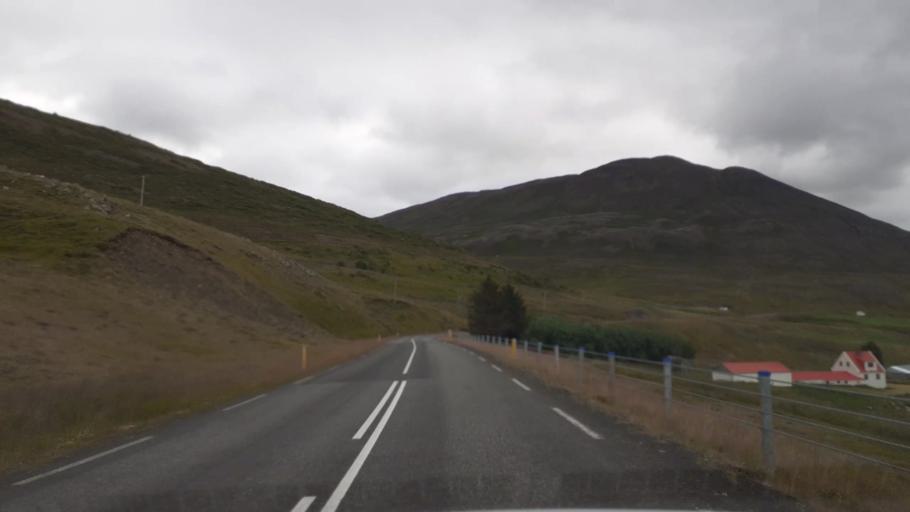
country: IS
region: Northeast
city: Akureyri
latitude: 65.8238
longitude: -18.0537
